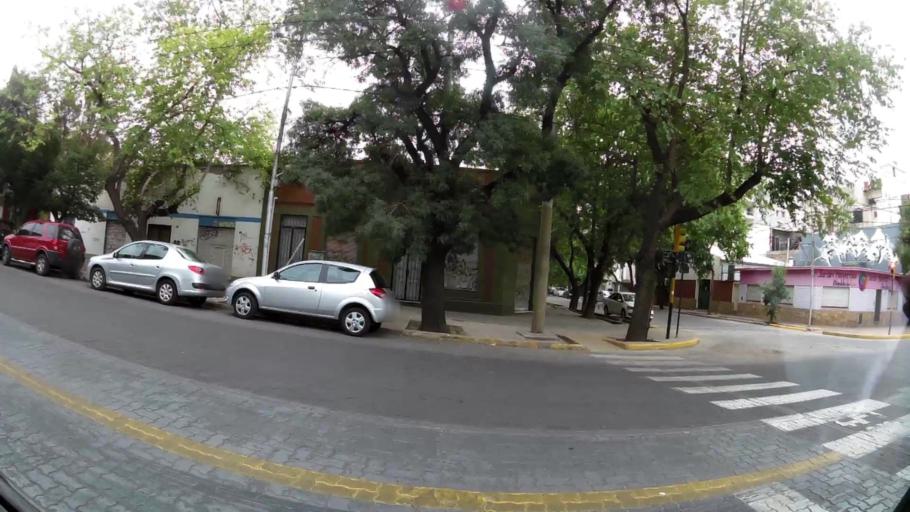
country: AR
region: Mendoza
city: Mendoza
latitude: -32.8841
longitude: -68.8503
